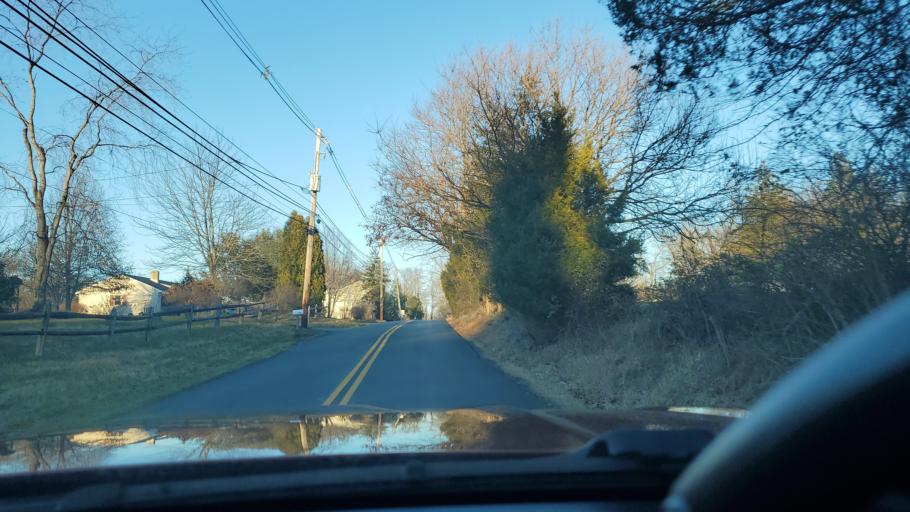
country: US
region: Pennsylvania
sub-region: Montgomery County
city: Woxall
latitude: 40.3124
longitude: -75.4968
